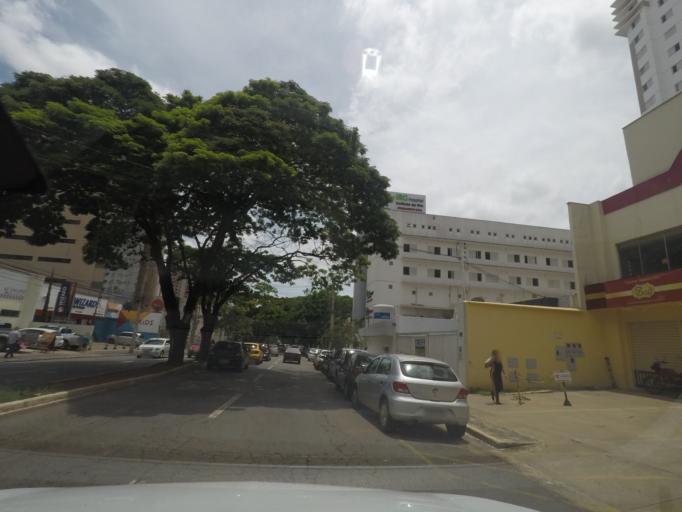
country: BR
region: Goias
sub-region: Goiania
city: Goiania
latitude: -16.6932
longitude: -49.2773
